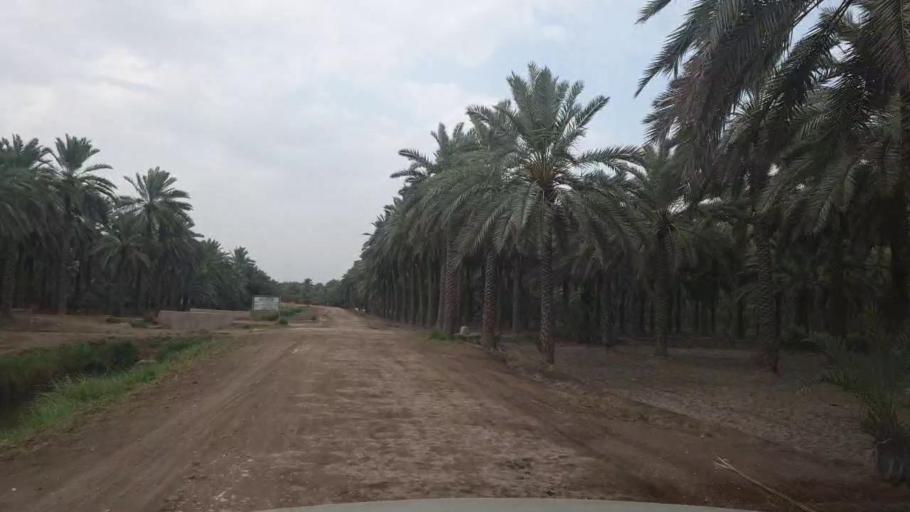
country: PK
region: Sindh
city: Sukkur
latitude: 27.6148
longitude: 68.8366
